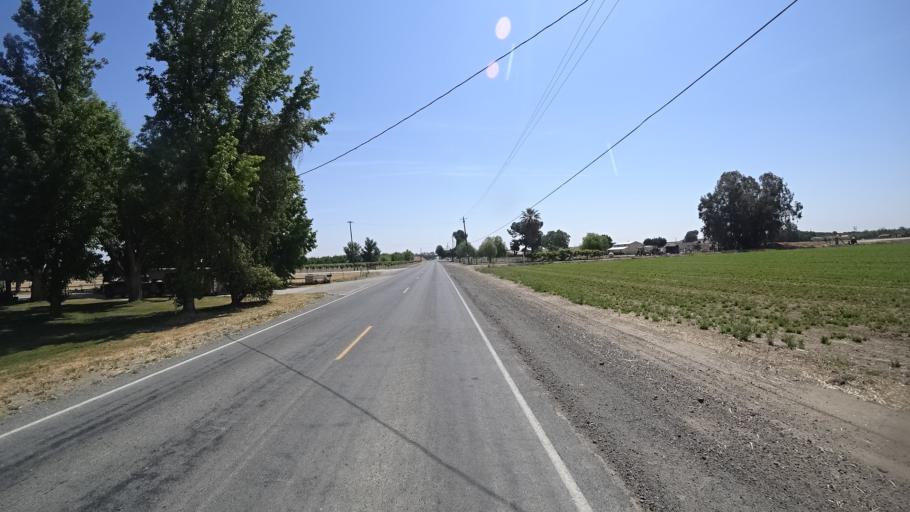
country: US
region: California
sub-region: Fresno County
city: Riverdale
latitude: 36.4020
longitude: -119.8127
